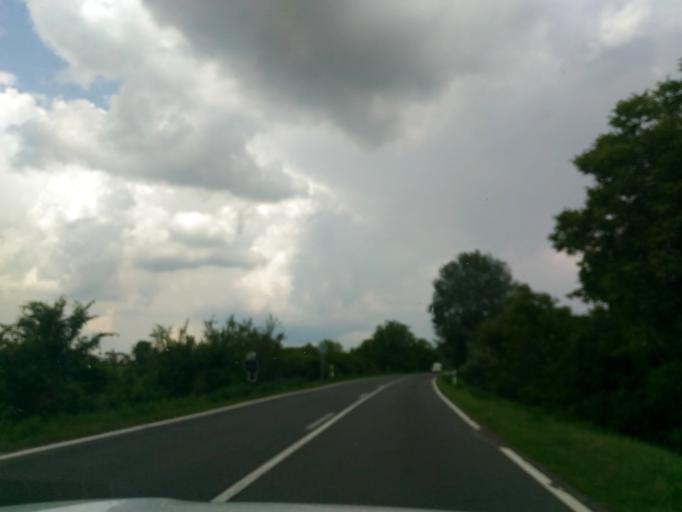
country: HU
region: Baranya
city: Hidas
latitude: 46.2744
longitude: 18.5152
